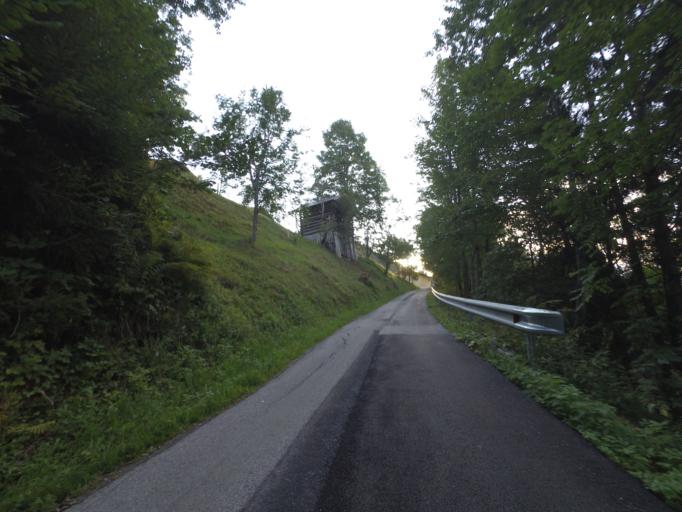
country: AT
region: Salzburg
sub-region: Politischer Bezirk Sankt Johann im Pongau
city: Goldegg
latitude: 47.3382
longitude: 13.1042
